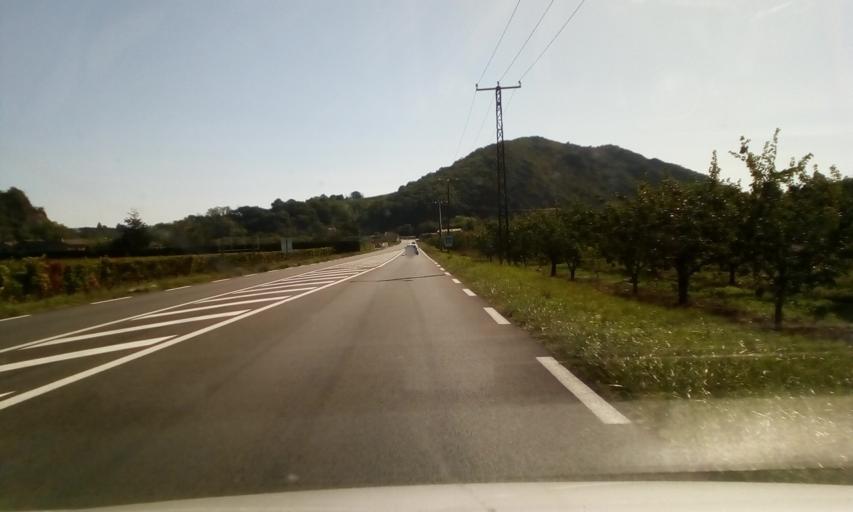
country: FR
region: Rhone-Alpes
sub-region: Departement de l'Ardeche
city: Saint-Jean-de-Muzols
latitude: 45.1009
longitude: 4.8314
